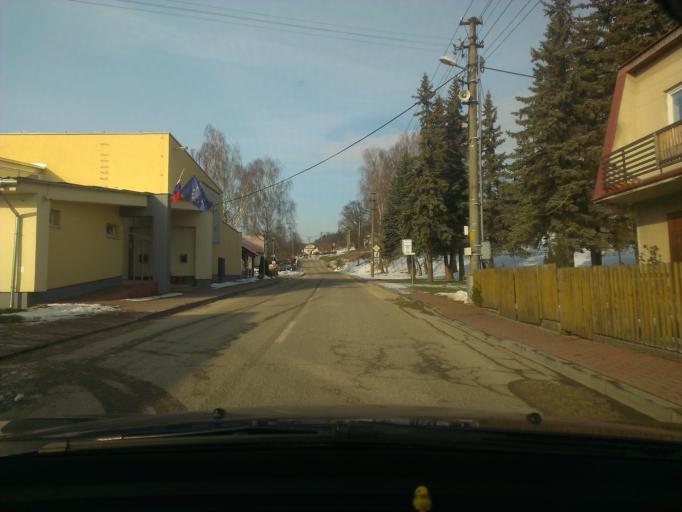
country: SK
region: Trenciansky
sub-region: Okres Myjava
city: Myjava
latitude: 48.7886
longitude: 17.5873
